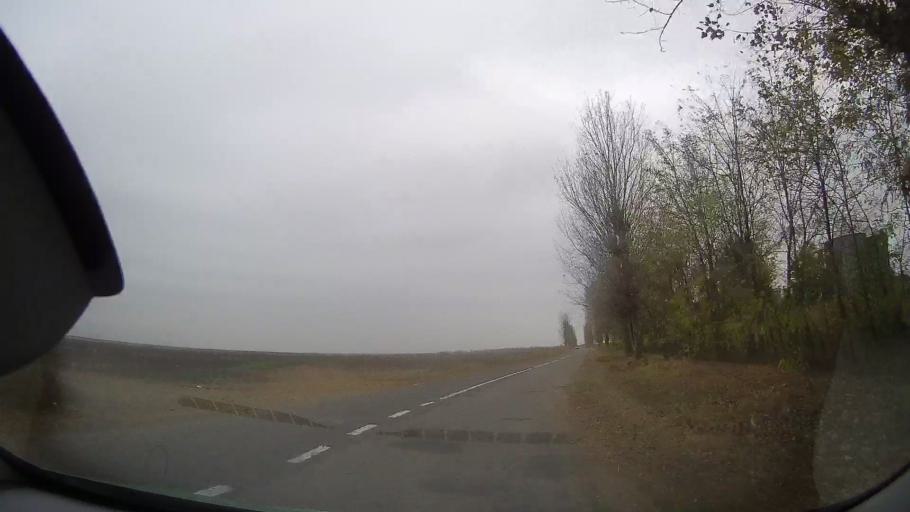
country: RO
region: Ialomita
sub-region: Comuna Valea Macrisului
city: Valea Macrisului
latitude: 44.7382
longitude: 26.8621
